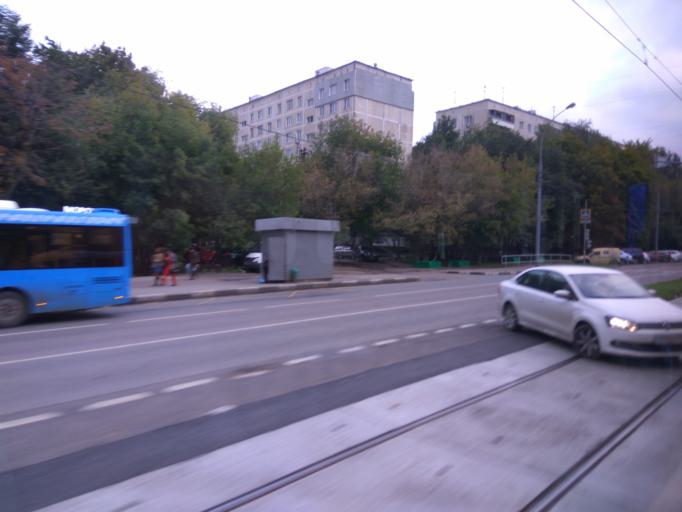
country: RU
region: Moscow
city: Chertanovo Yuzhnoye
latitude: 55.6029
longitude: 37.5894
